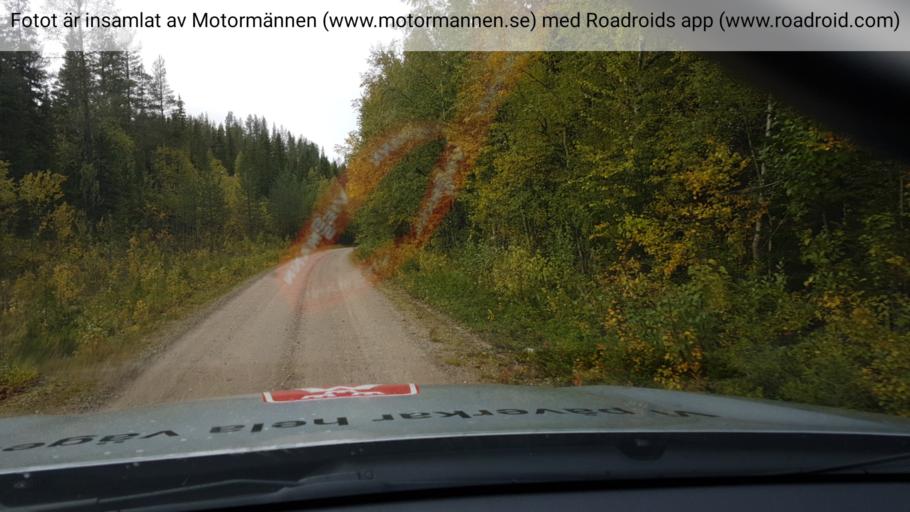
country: SE
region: Jaemtland
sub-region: Harjedalens Kommun
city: Sveg
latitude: 62.2474
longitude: 13.2955
